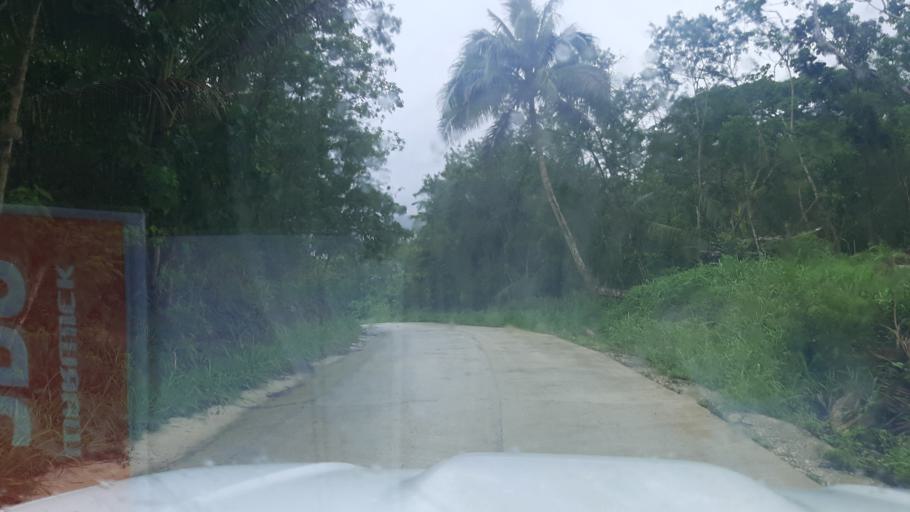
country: VU
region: Shefa
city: Port-Vila
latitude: -17.6376
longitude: 168.2120
